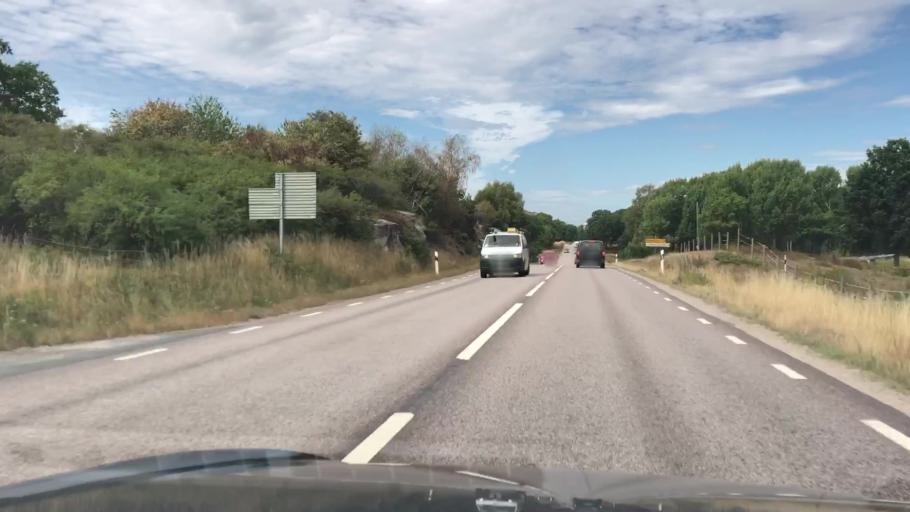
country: SE
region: Blekinge
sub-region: Karlskrona Kommun
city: Sturko
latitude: 56.1888
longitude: 15.7098
